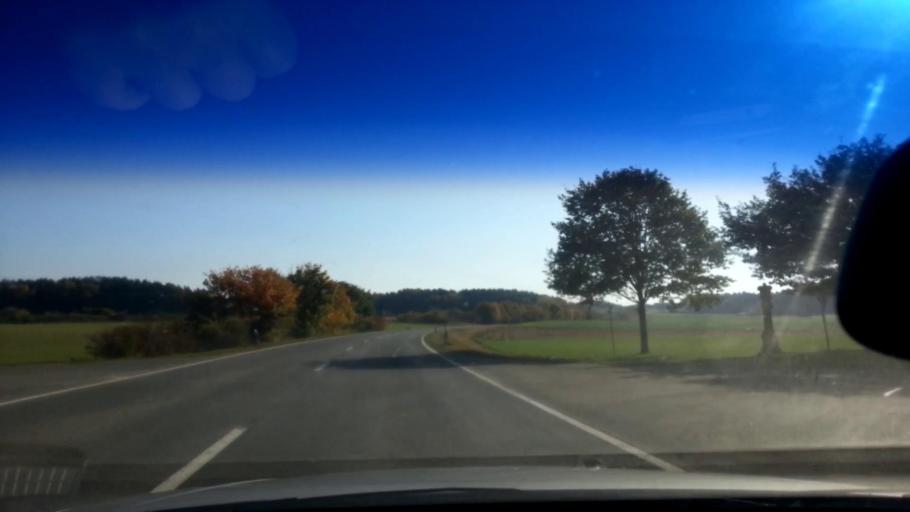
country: DE
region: Bavaria
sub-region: Upper Franconia
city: Stadelhofen
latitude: 49.9956
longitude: 11.2178
